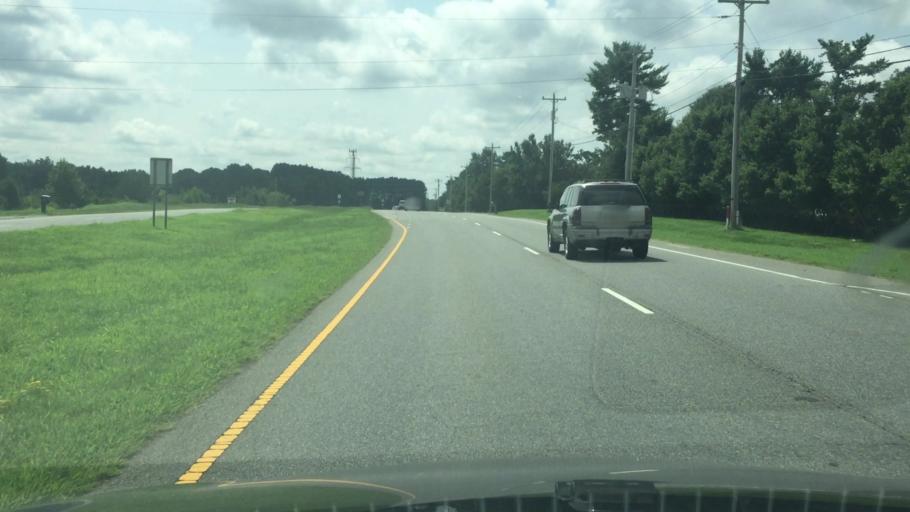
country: US
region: North Carolina
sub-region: Cabarrus County
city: Kannapolis
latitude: 35.4762
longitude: -80.6727
